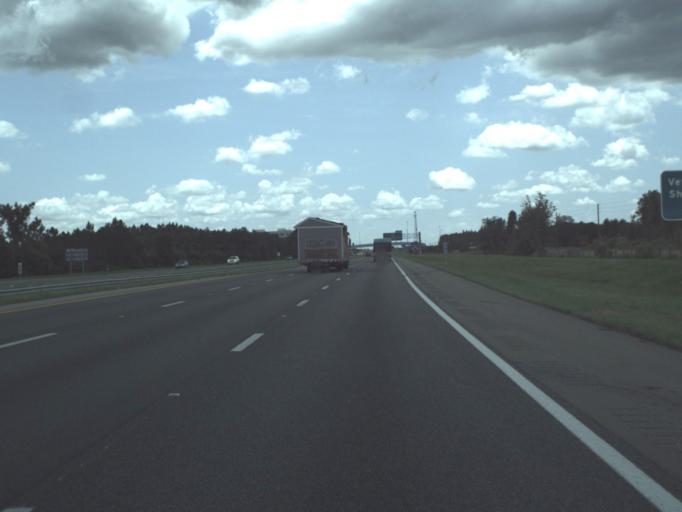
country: US
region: Florida
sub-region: Hillsborough County
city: Pebble Creek
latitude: 28.1385
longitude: -82.3802
